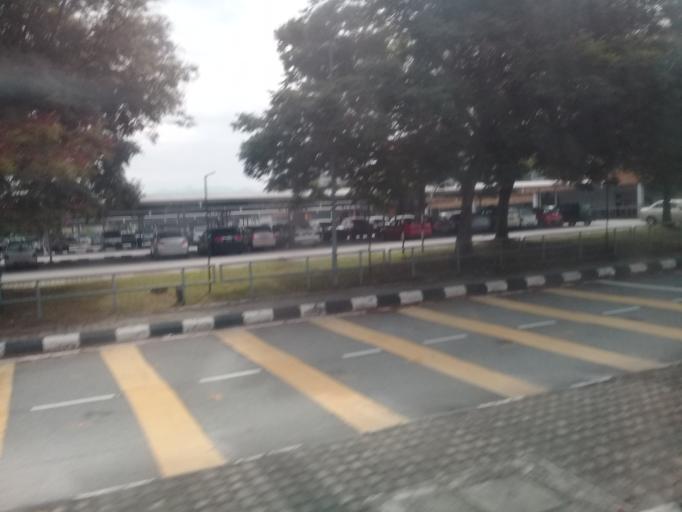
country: MY
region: Perak
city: Ipoh
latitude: 4.6164
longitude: 101.1174
